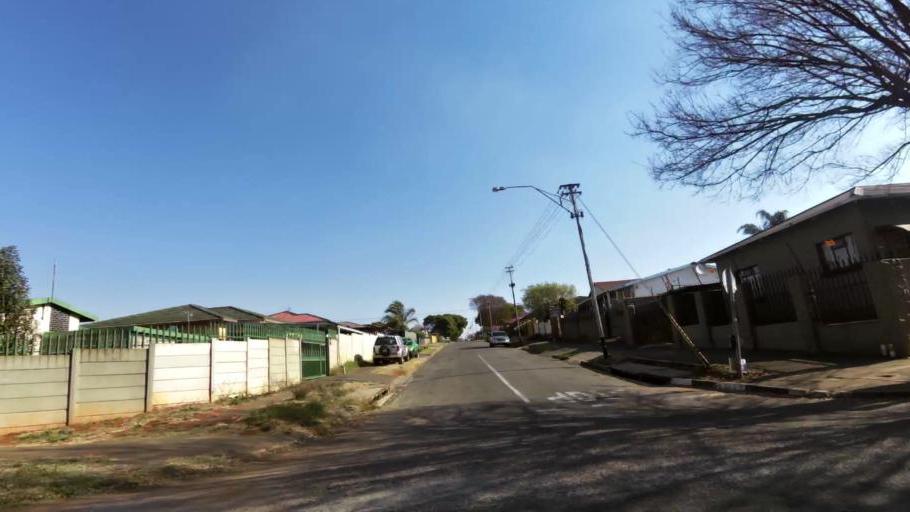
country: ZA
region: Gauteng
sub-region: City of Johannesburg Metropolitan Municipality
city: Johannesburg
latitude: -26.1711
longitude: 27.9677
